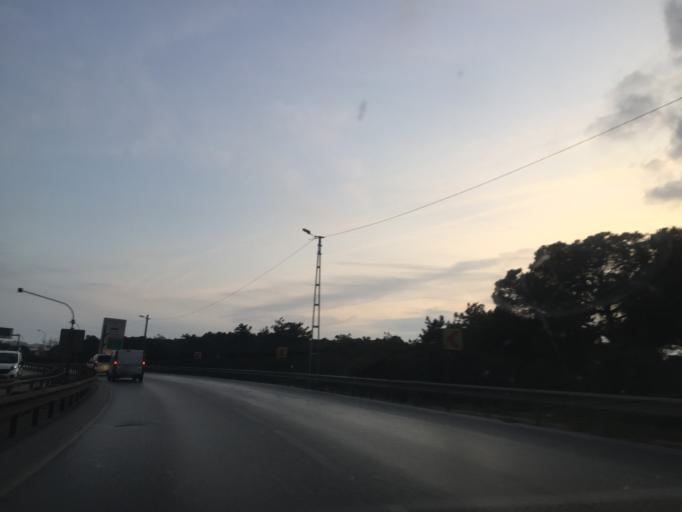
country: TR
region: Istanbul
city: Samandira
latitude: 40.9740
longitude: 29.2189
